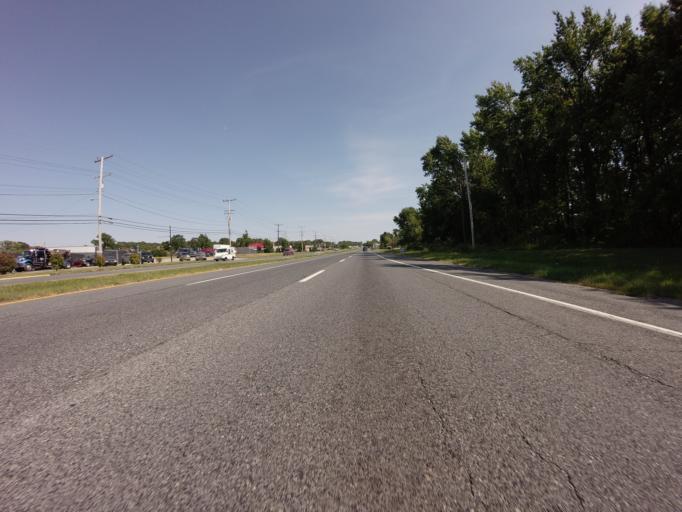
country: US
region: Maryland
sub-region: Baltimore County
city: Edgemere
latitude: 39.2650
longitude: -76.4668
